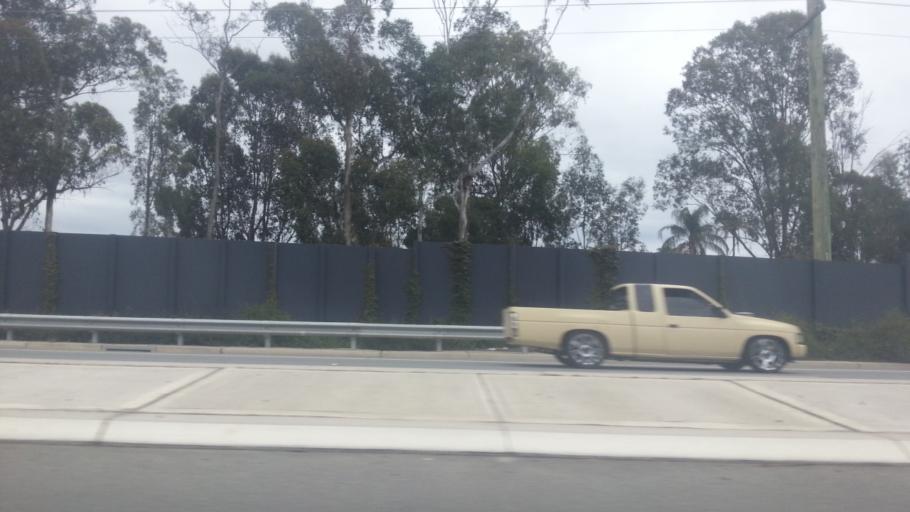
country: AU
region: New South Wales
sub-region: Penrith Municipality
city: Werrington Downs
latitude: -33.7292
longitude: 150.7197
